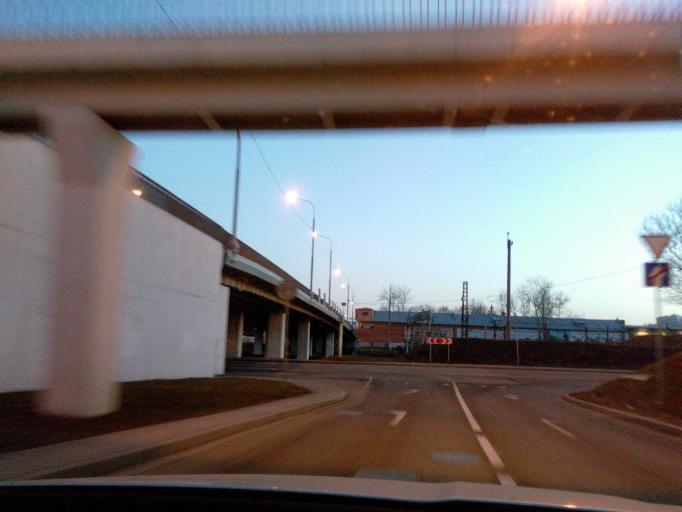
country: RU
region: Moscow
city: Zelenograd
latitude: 55.9764
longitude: 37.1850
